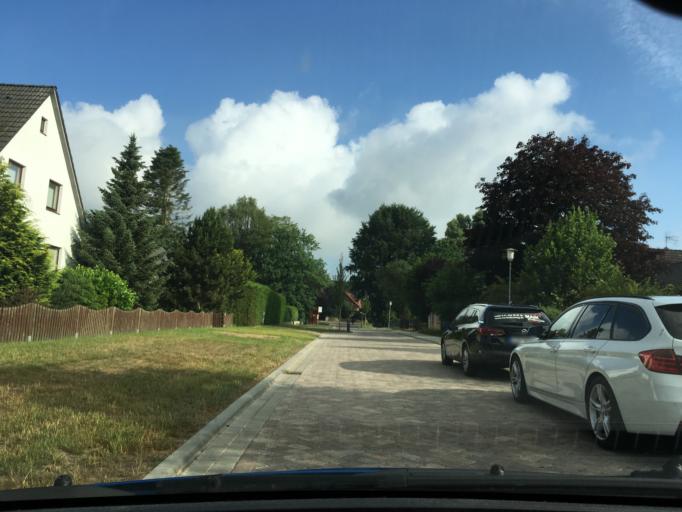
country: DE
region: Lower Saxony
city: Kakenstorf
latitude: 53.3107
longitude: 9.7743
